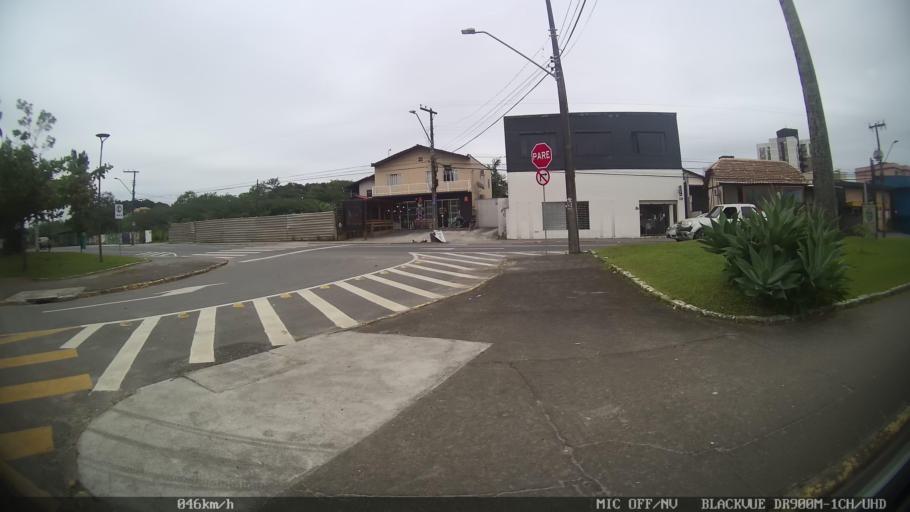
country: BR
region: Santa Catarina
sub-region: Joinville
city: Joinville
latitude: -26.3240
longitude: -48.8450
